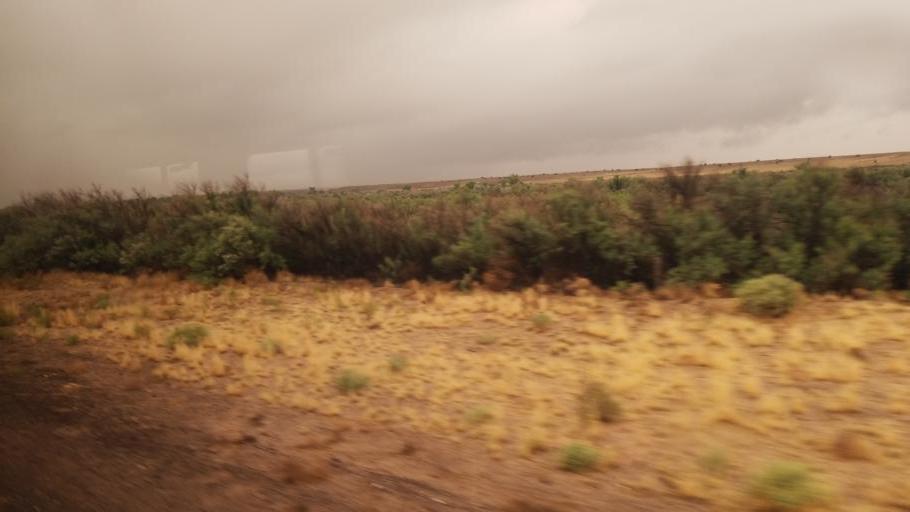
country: US
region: Arizona
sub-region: Navajo County
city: Joseph City
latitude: 34.9615
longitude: -110.3932
